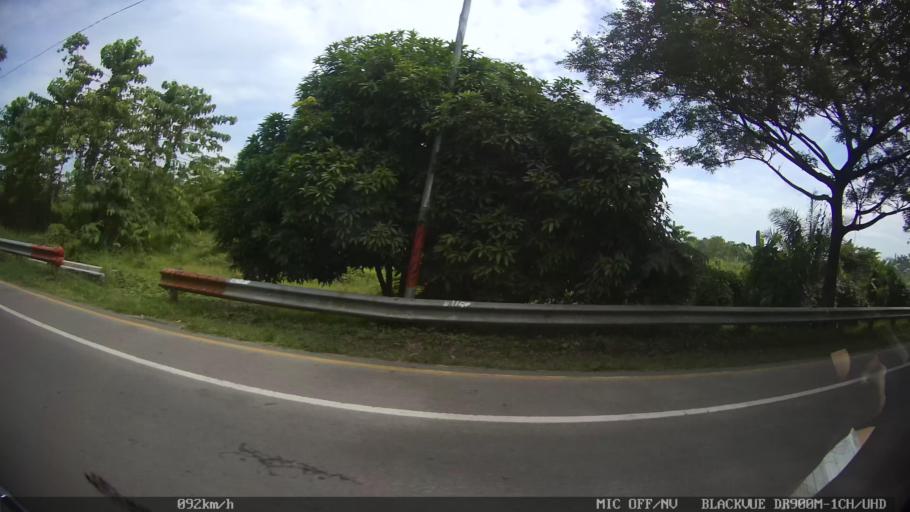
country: ID
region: North Sumatra
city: Percut
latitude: 3.5992
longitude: 98.8281
